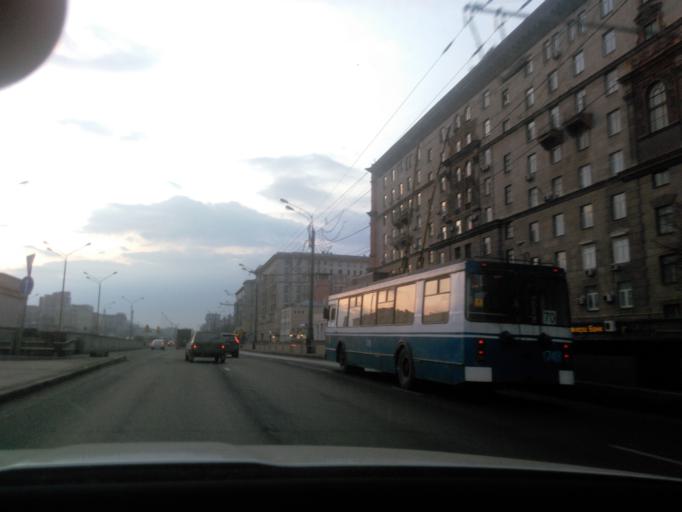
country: RU
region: Moscow
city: Sokol
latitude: 55.8053
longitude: 37.5126
